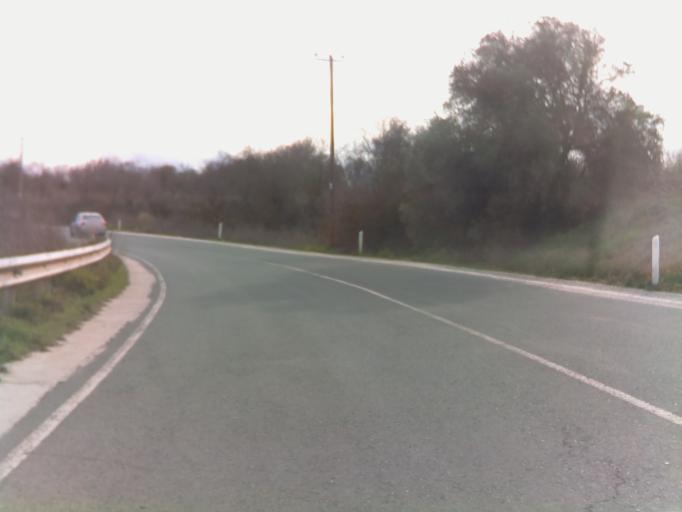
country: CY
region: Pafos
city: Pegeia
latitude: 34.9424
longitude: 32.4108
